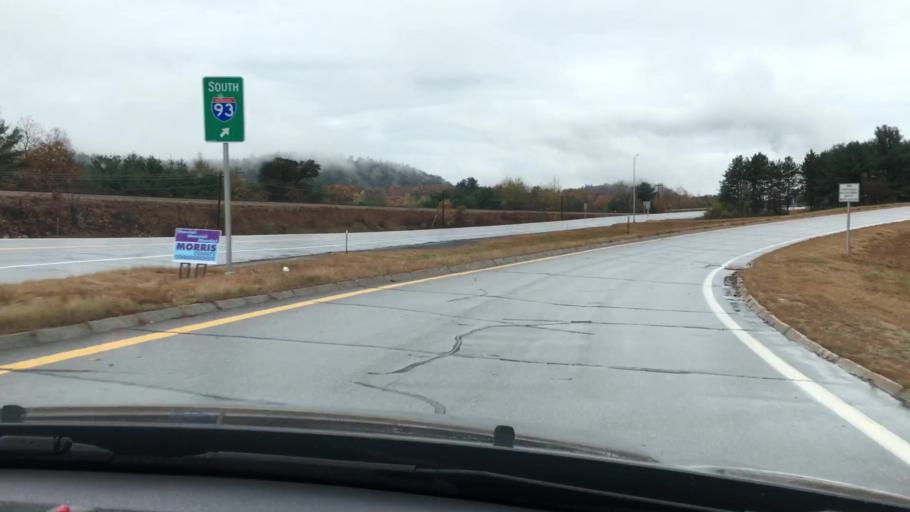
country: US
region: New Hampshire
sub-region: Grafton County
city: Ashland
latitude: 43.6982
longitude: -71.6486
